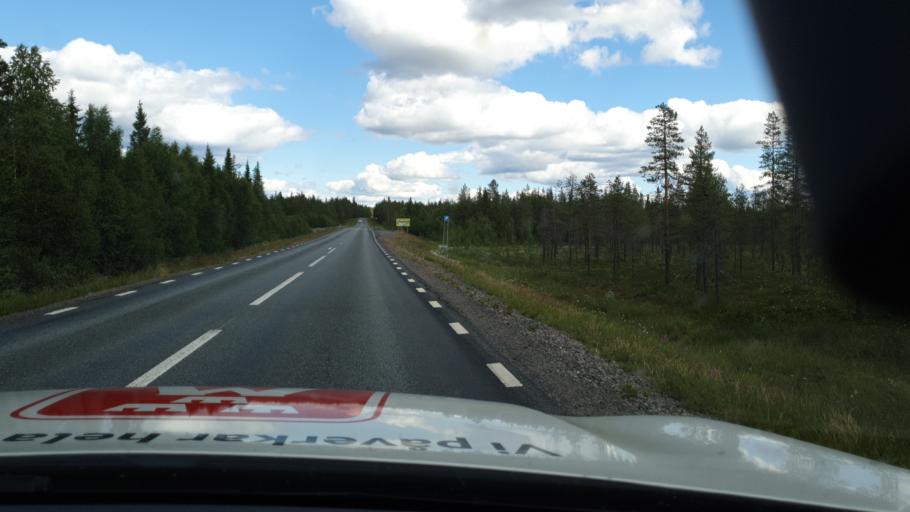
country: SE
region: Vaesterbotten
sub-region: Sorsele Kommun
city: Sorsele
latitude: 65.5652
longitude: 17.9946
